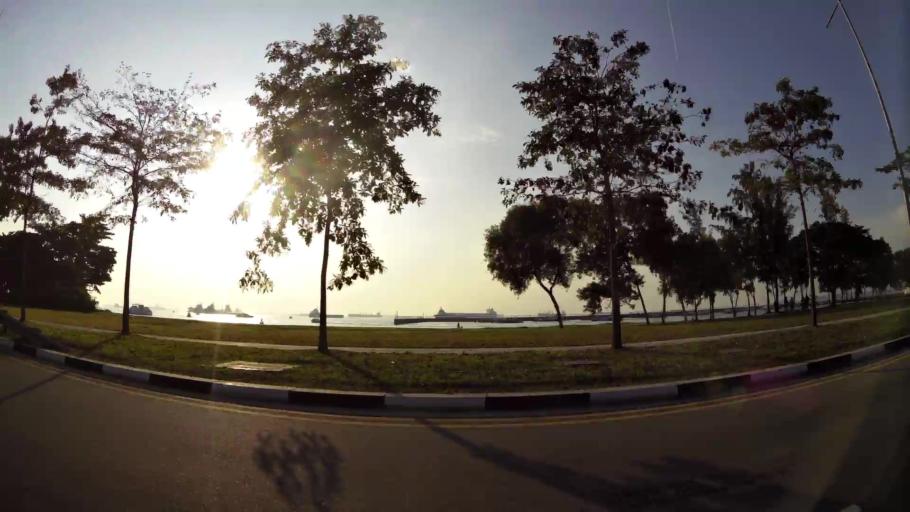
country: SG
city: Singapore
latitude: 1.2730
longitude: 103.8653
